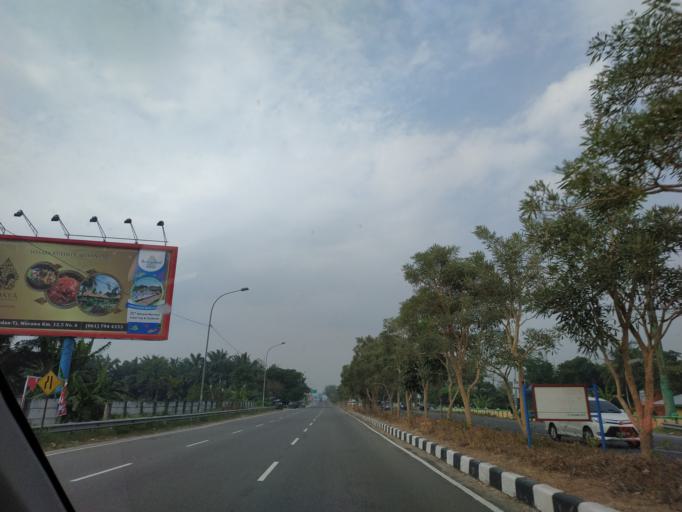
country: ID
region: North Sumatra
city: Percut
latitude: 3.6049
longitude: 98.8489
